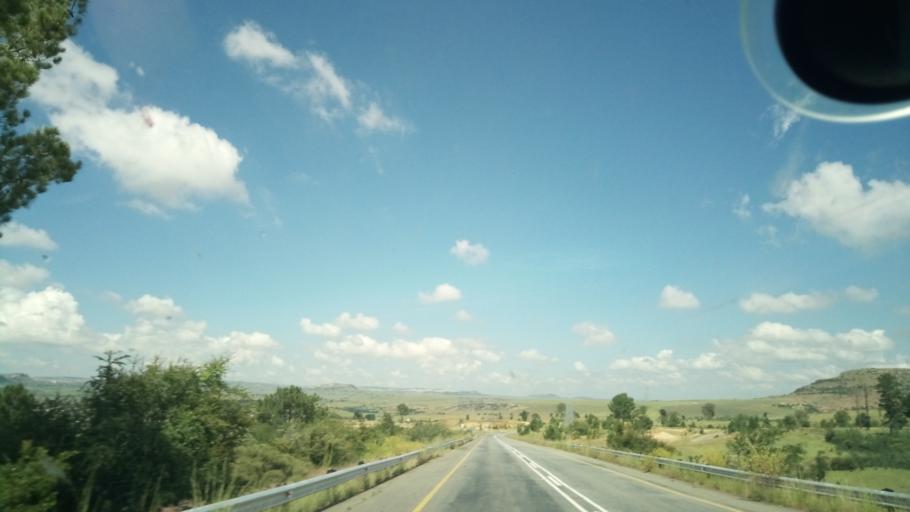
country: ZA
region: Orange Free State
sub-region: Thabo Mofutsanyana District Municipality
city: Ficksburg
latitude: -28.8856
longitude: 27.8648
